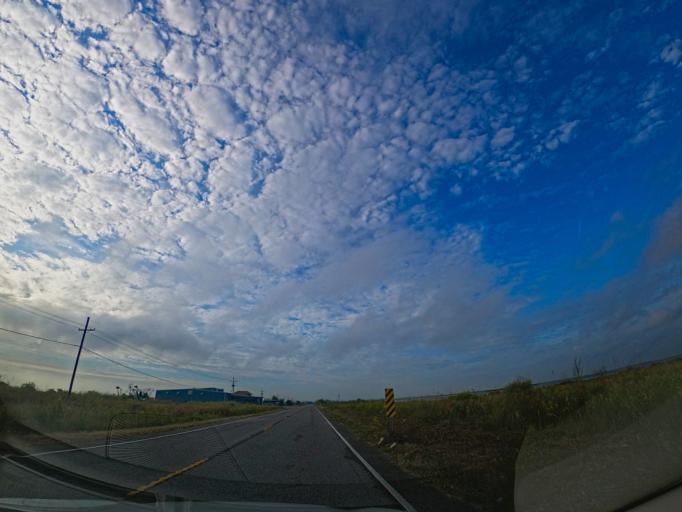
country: US
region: Louisiana
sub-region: Terrebonne Parish
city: Chauvin
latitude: 29.3617
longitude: -90.6260
